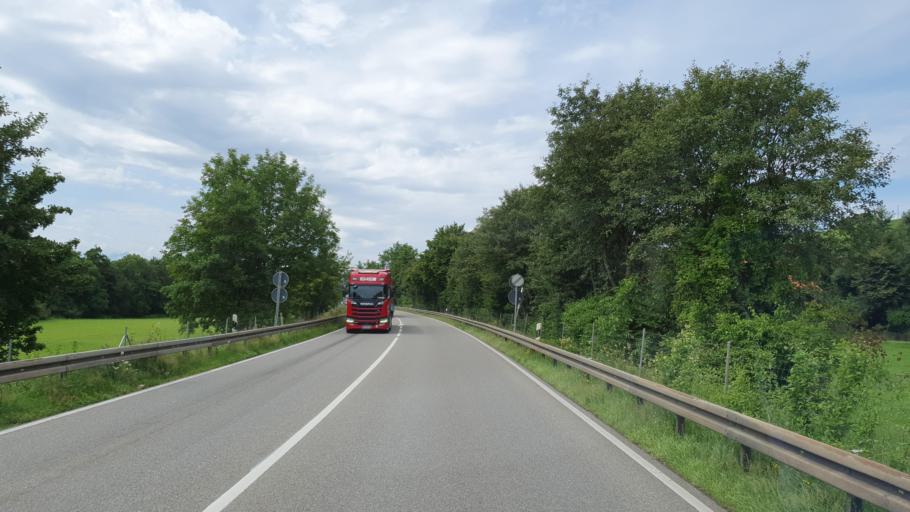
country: DE
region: Bavaria
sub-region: Swabia
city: Weissensberg
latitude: 47.5780
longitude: 9.7314
